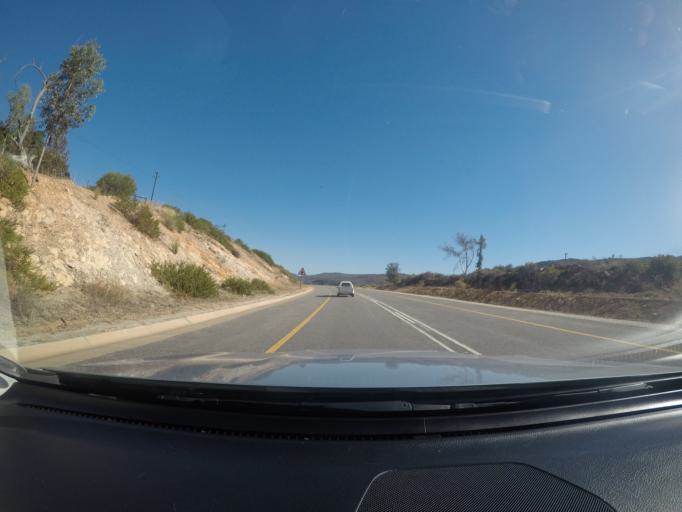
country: ZA
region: Western Cape
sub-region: West Coast District Municipality
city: Clanwilliam
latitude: -32.4316
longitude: 18.9554
